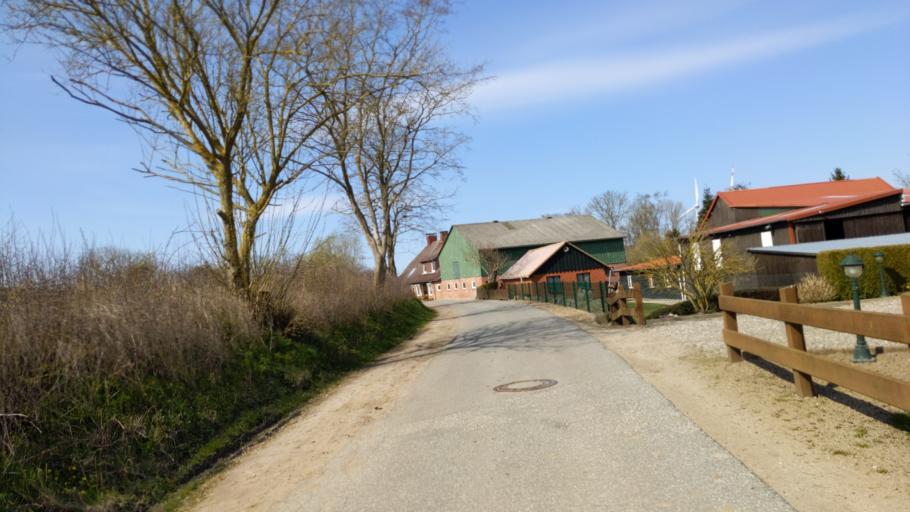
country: DE
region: Schleswig-Holstein
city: Schashagen
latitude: 54.1325
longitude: 10.8845
